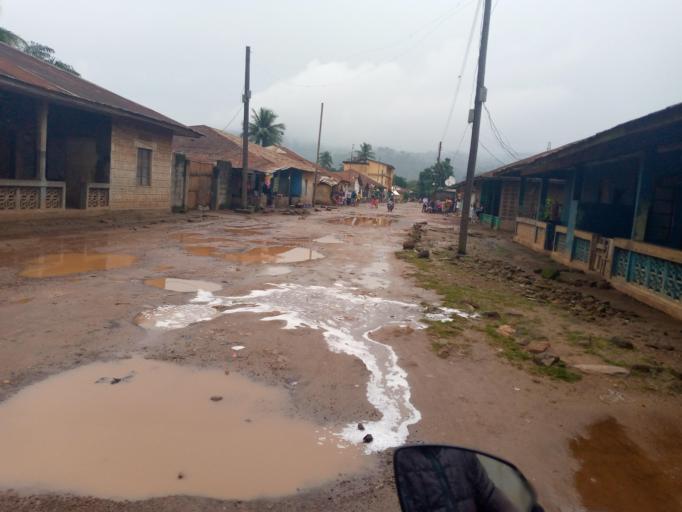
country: SL
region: Eastern Province
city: Kenema
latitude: 7.8804
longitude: -11.1854
